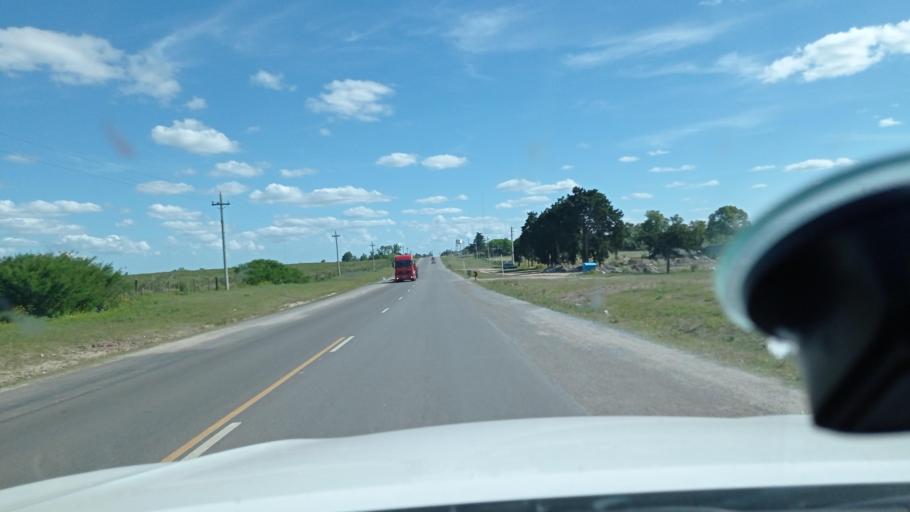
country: UY
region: Florida
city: Florida
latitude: -34.0804
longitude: -56.2355
